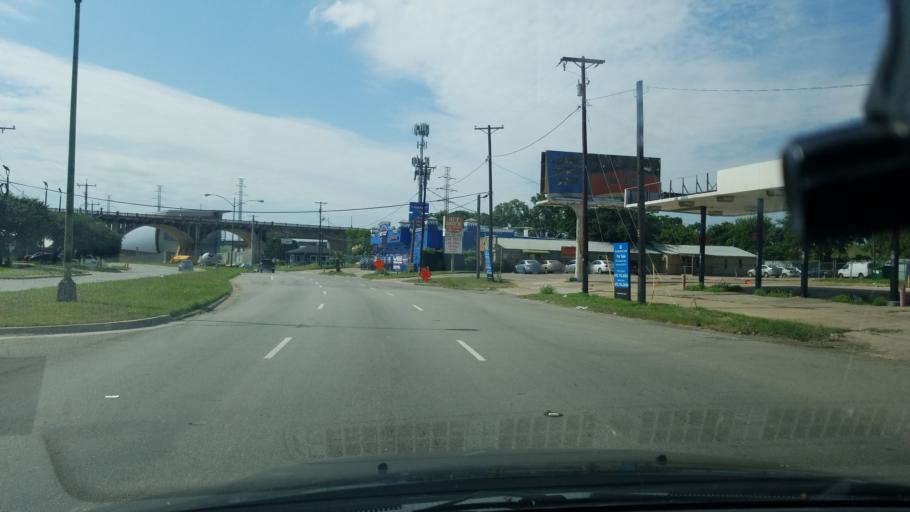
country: US
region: Texas
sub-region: Dallas County
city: Dallas
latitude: 32.7703
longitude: -96.8115
